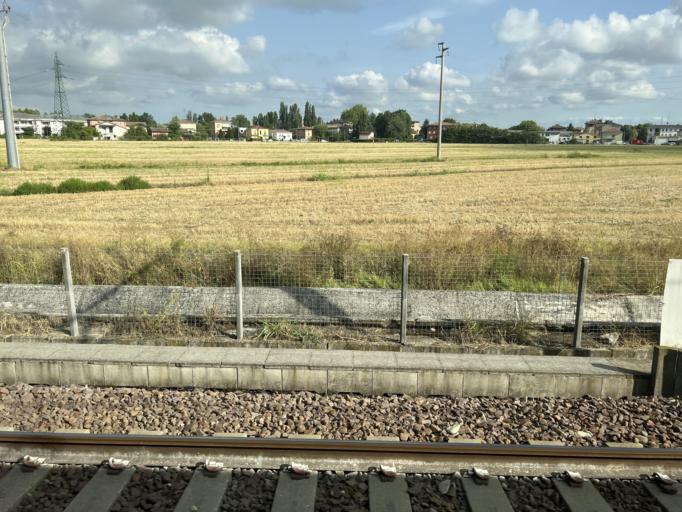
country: IT
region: Emilia-Romagna
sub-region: Provincia di Parma
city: Parma
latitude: 44.8197
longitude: 10.3499
